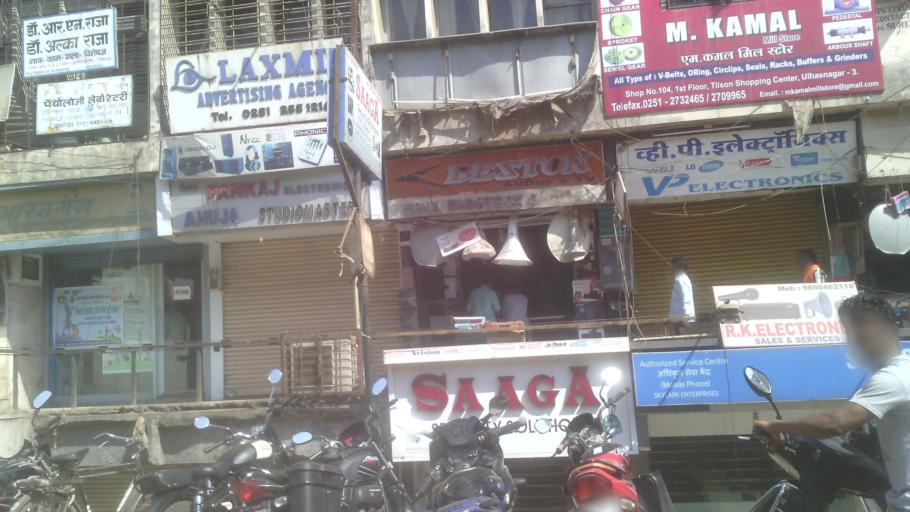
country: IN
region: Maharashtra
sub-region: Thane
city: Ulhasnagar
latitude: 19.2283
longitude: 73.1588
